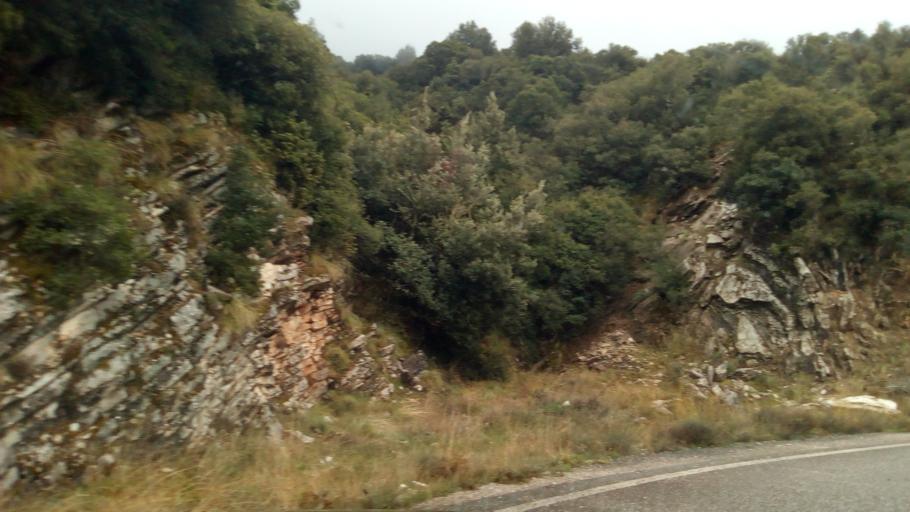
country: GR
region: West Greece
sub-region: Nomos Aitolias kai Akarnanias
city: Nafpaktos
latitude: 38.5138
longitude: 21.8420
